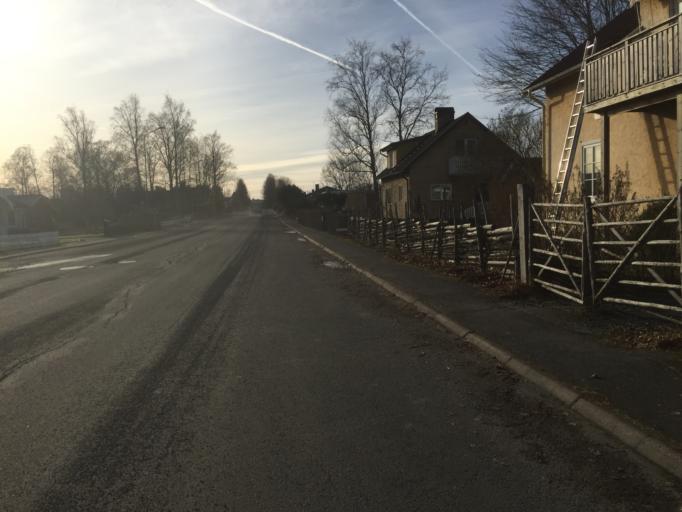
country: SE
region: Joenkoeping
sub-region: Aneby Kommun
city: Aneby
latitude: 57.8340
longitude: 14.8100
